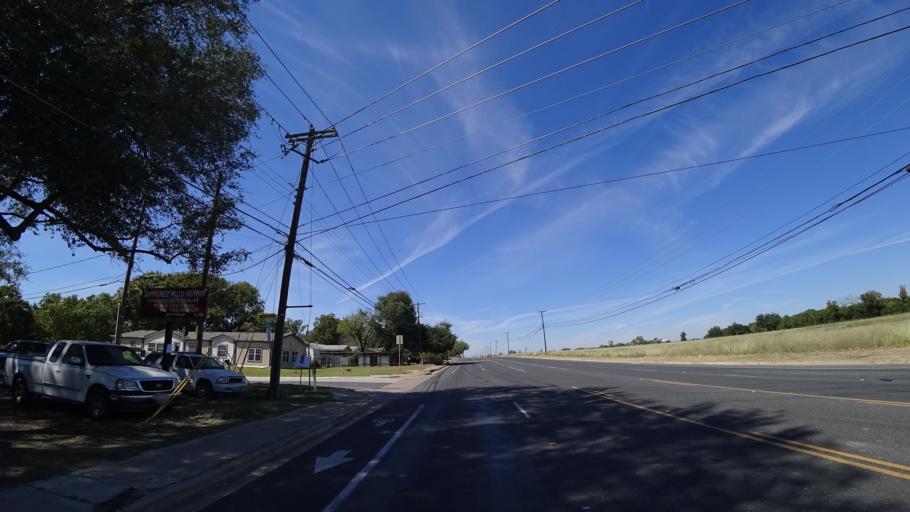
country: US
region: Texas
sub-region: Travis County
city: Austin
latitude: 30.1924
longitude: -97.6989
